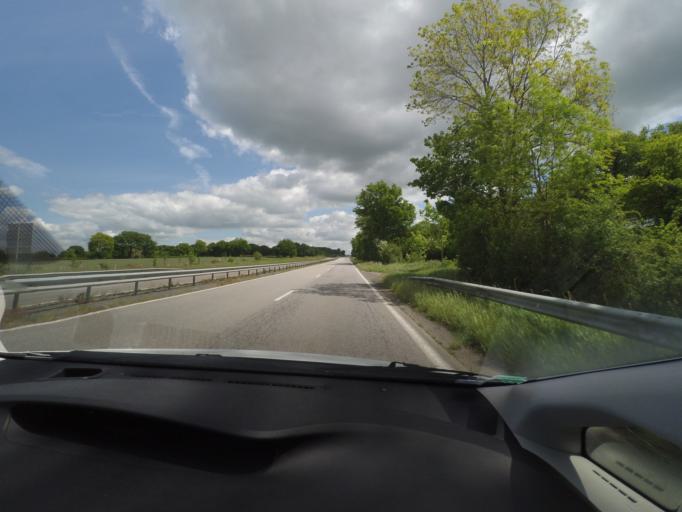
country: FR
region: Poitou-Charentes
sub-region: Departement des Deux-Sevres
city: La Peyratte
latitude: 46.6513
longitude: -0.1384
